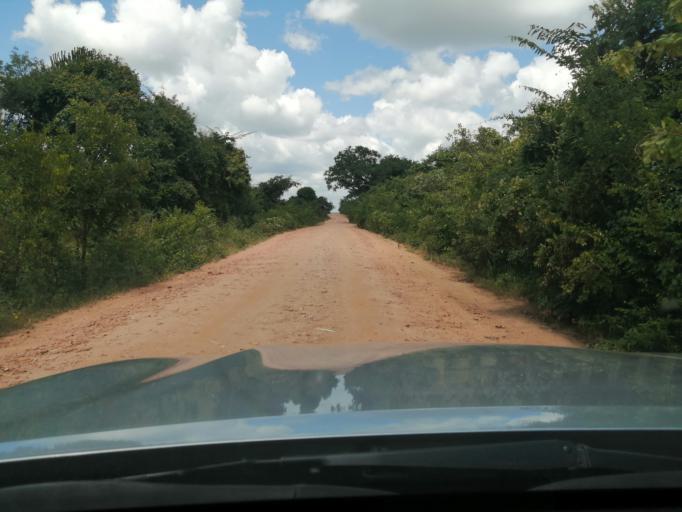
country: ZM
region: Lusaka
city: Lusaka
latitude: -15.1704
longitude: 27.9449
